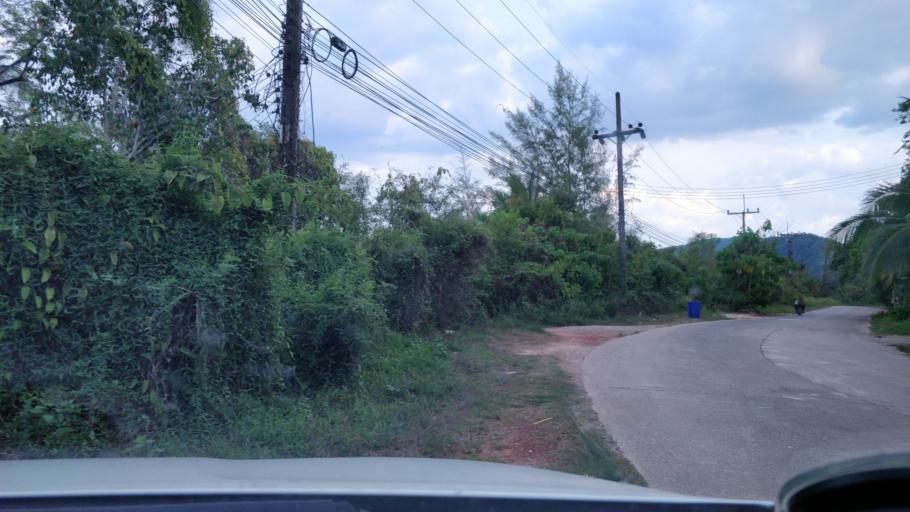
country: TH
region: Krabi
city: Ko Lanta
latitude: 7.5761
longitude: 99.0690
